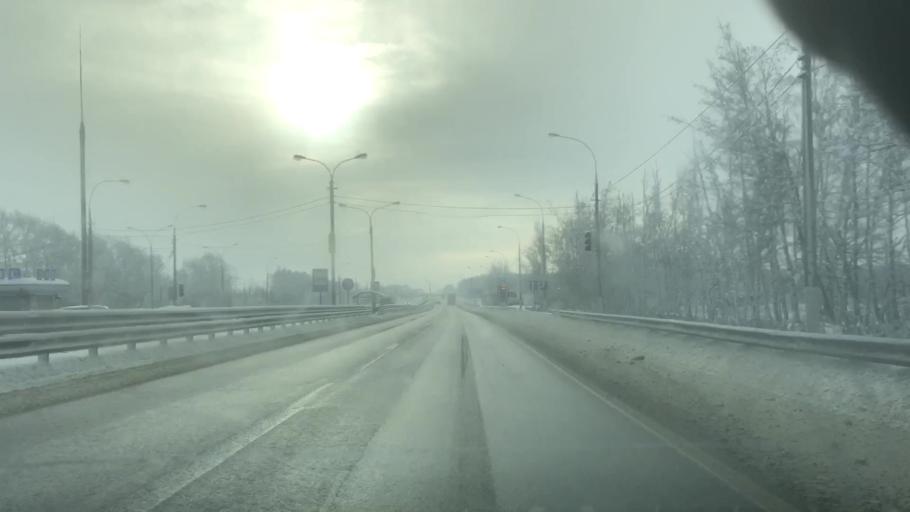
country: RU
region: Tula
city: Venev
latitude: 54.3439
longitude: 38.1545
